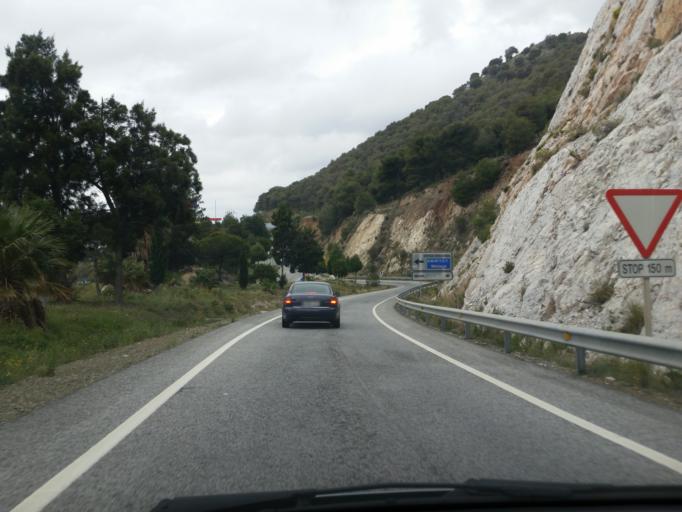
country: ES
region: Andalusia
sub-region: Provincia de Malaga
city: Benalmadena
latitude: 36.5874
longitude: -4.5943
